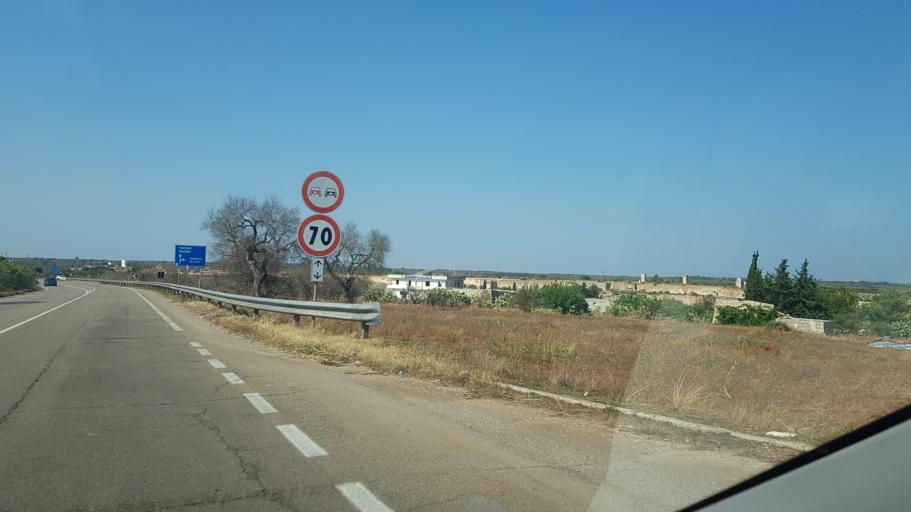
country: IT
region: Apulia
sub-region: Provincia di Lecce
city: Acquarica del Capo
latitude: 39.9221
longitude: 18.2359
